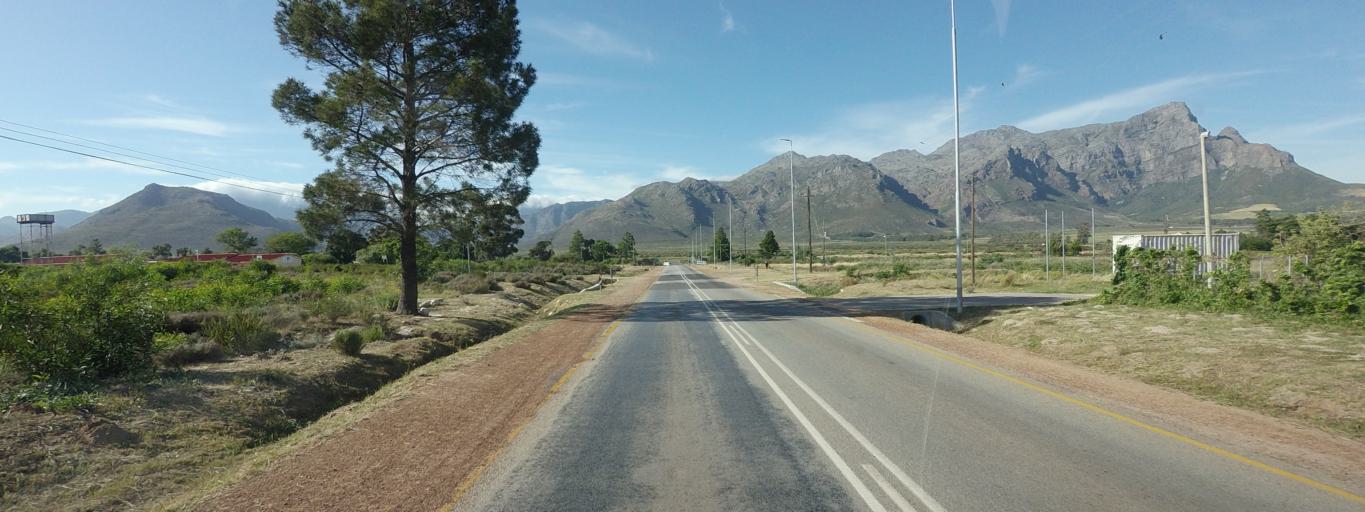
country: ZA
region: Western Cape
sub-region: Cape Winelands District Municipality
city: Paarl
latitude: -33.8755
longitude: 19.0447
